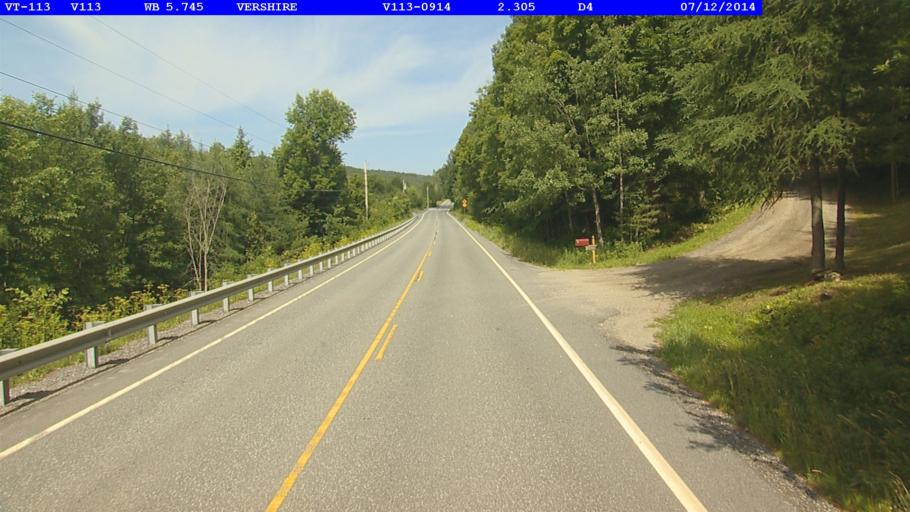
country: US
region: Vermont
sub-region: Orange County
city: Chelsea
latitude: 43.9749
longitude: -72.3460
